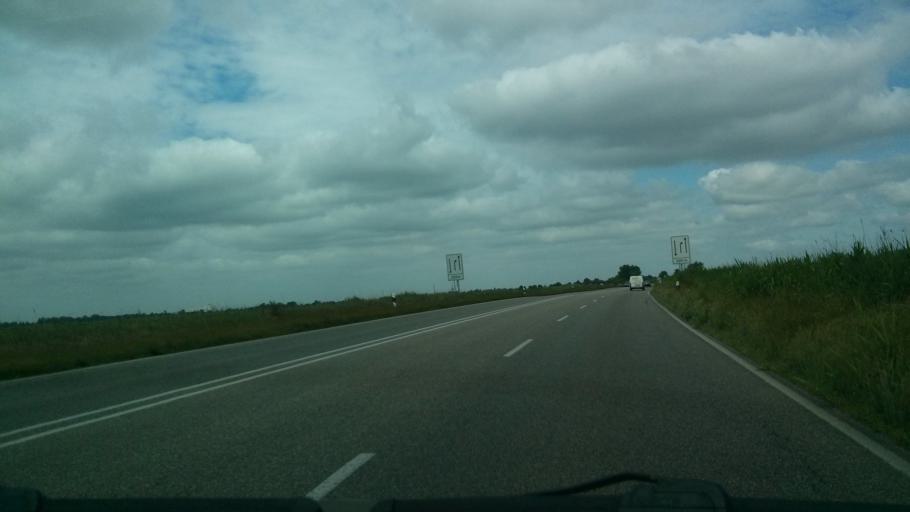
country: DE
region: Lower Saxony
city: Sandstedt
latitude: 53.4341
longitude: 8.5473
